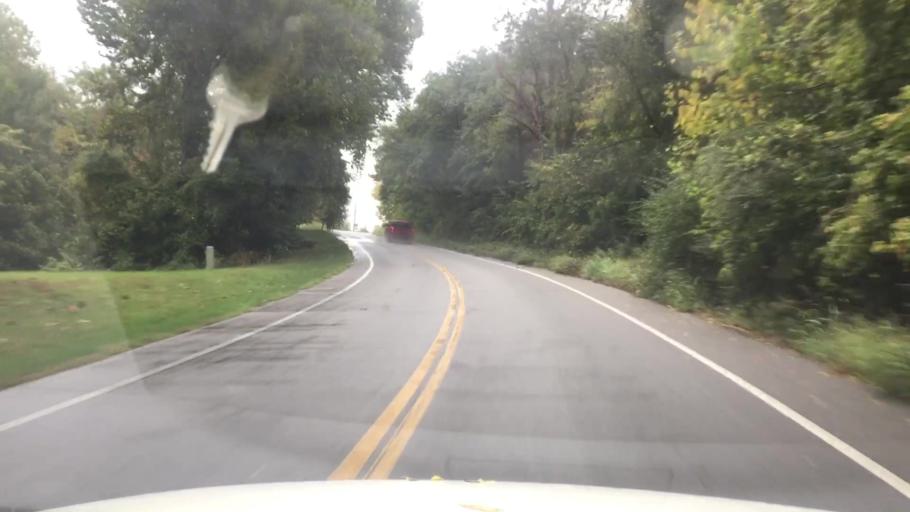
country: US
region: Missouri
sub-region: Boone County
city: Columbia
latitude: 38.8857
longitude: -92.4349
